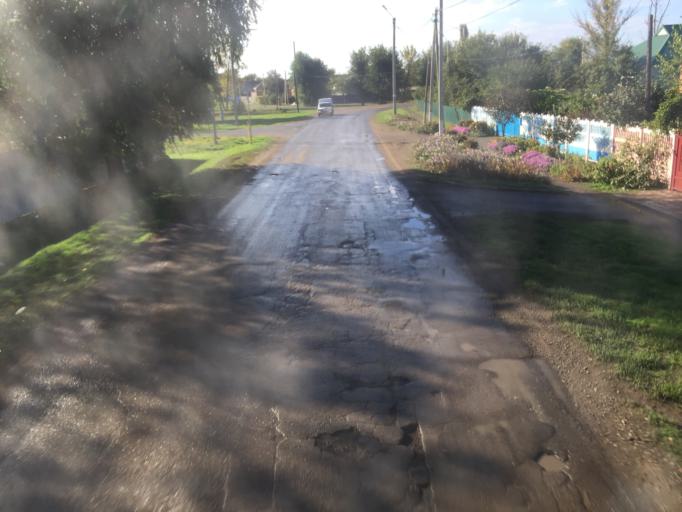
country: RU
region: Rostov
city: Peschanokopskoye
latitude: 46.1901
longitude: 41.0823
